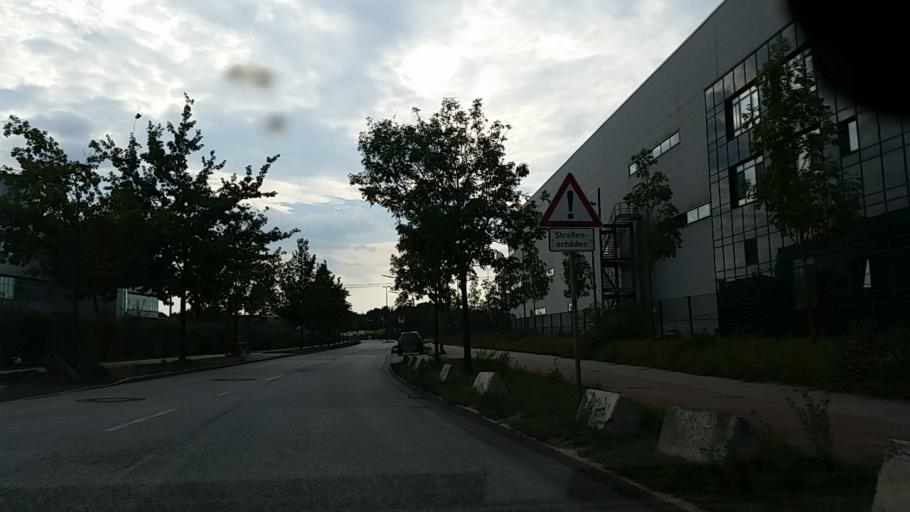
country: DE
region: Hamburg
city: Wandsbek
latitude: 53.4979
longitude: 10.1023
